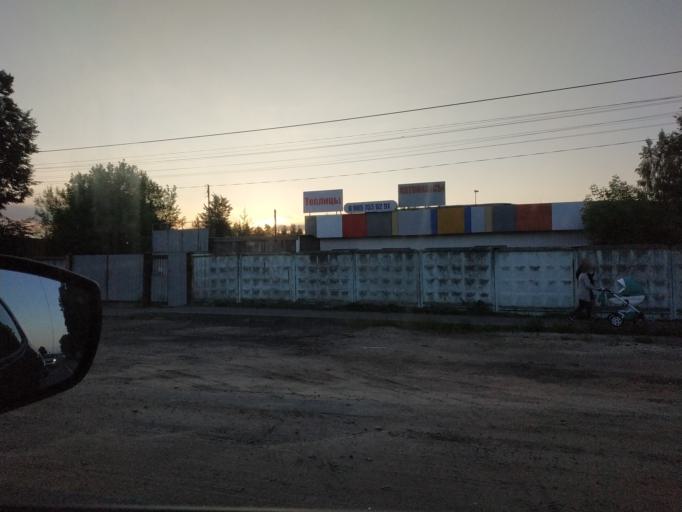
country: RU
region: Moskovskaya
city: Chernogolovka
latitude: 56.0645
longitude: 38.2613
